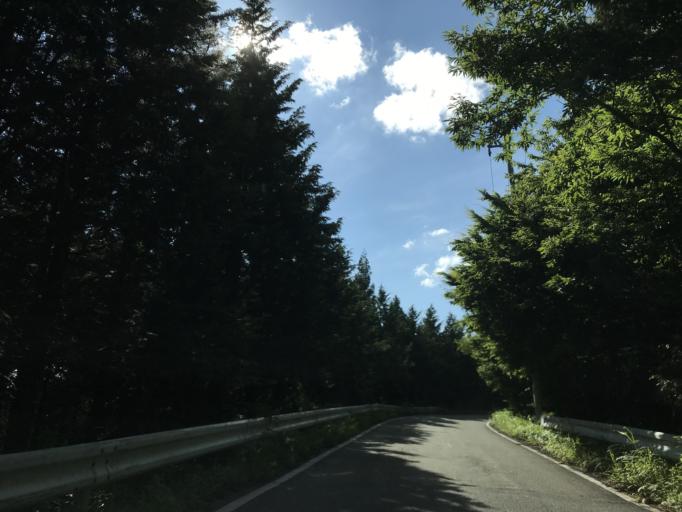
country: JP
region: Iwate
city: Ichinoseki
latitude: 38.8918
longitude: 140.9003
